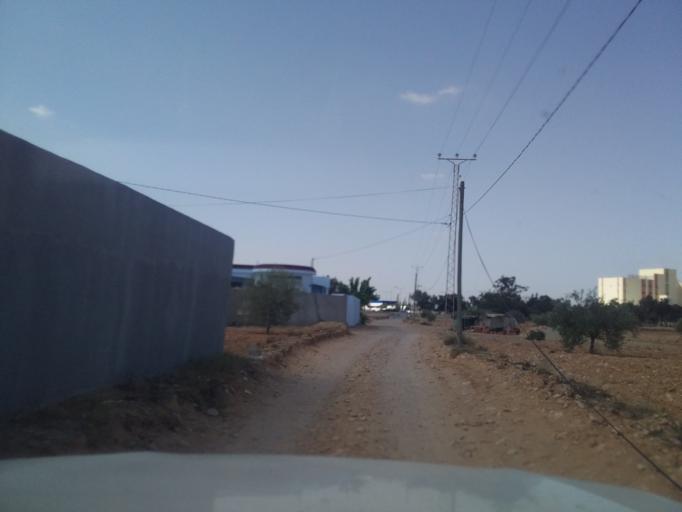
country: TN
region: Madanin
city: Medenine
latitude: 33.5999
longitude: 10.3122
